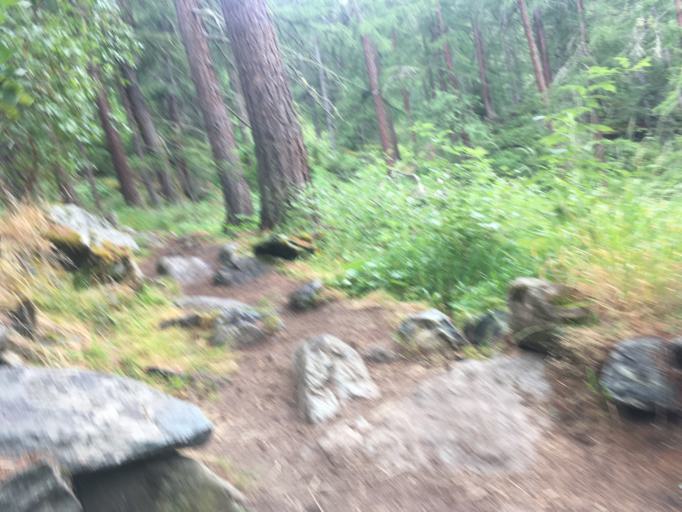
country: CH
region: Valais
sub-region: Visp District
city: Zermatt
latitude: 46.0065
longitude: 7.7378
